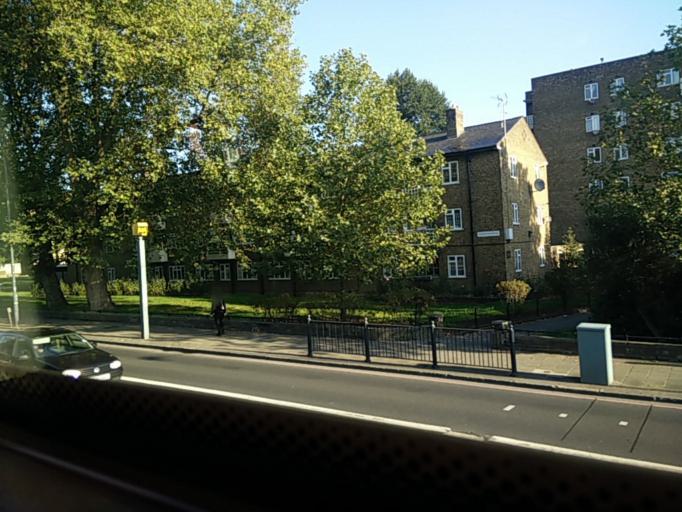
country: GB
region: England
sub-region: Greater London
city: Poplar
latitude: 51.5111
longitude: -0.0239
